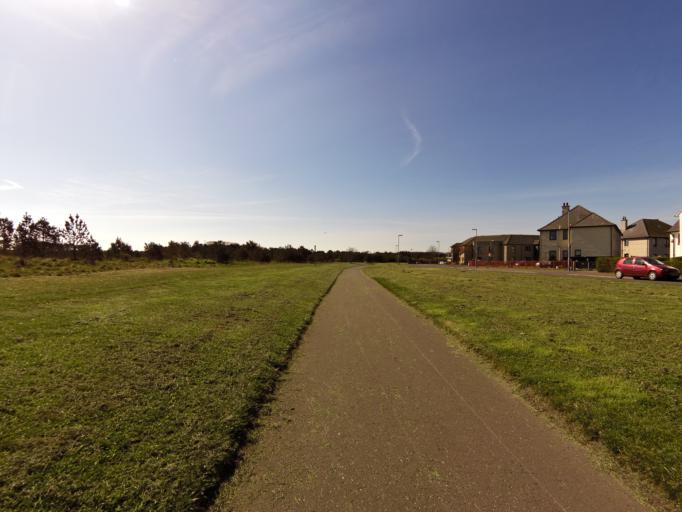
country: GB
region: Scotland
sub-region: Angus
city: Montrose
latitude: 56.7113
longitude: -2.4539
